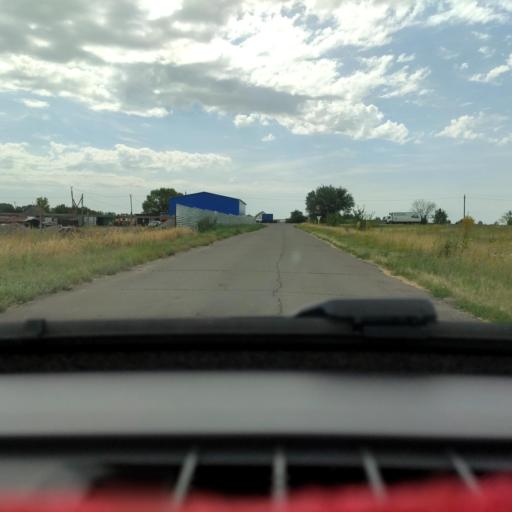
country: RU
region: Voronezj
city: Davydovka
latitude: 51.1936
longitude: 39.4939
